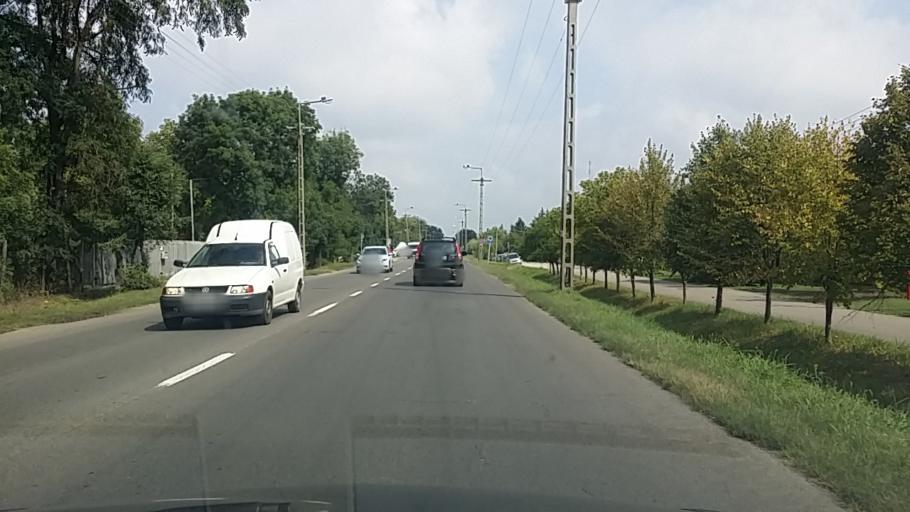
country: HU
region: Csongrad
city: Szeged
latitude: 46.2832
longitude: 20.1700
